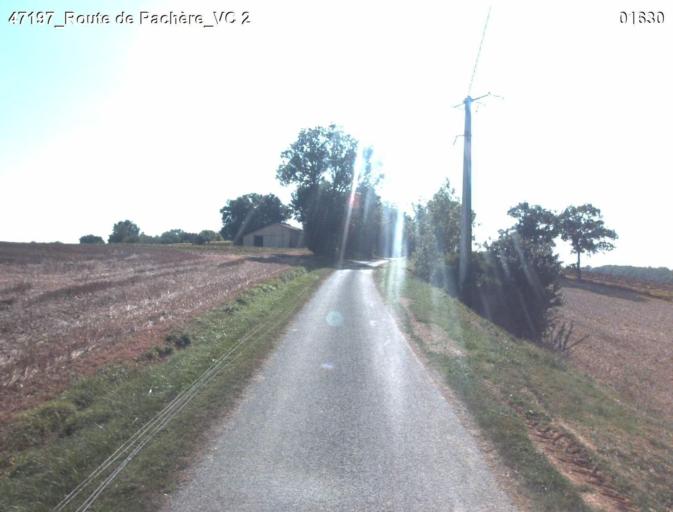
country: FR
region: Aquitaine
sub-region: Departement du Lot-et-Garonne
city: Laplume
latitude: 44.0895
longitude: 0.4544
